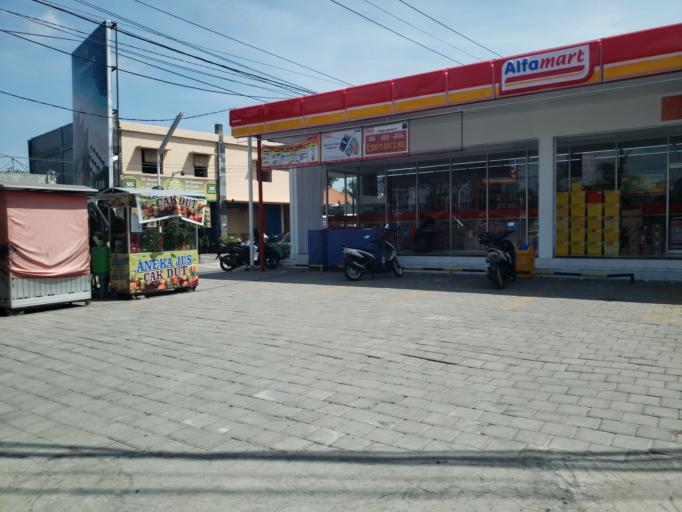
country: ID
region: Bali
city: Jimbaran
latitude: -8.8195
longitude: 115.1532
